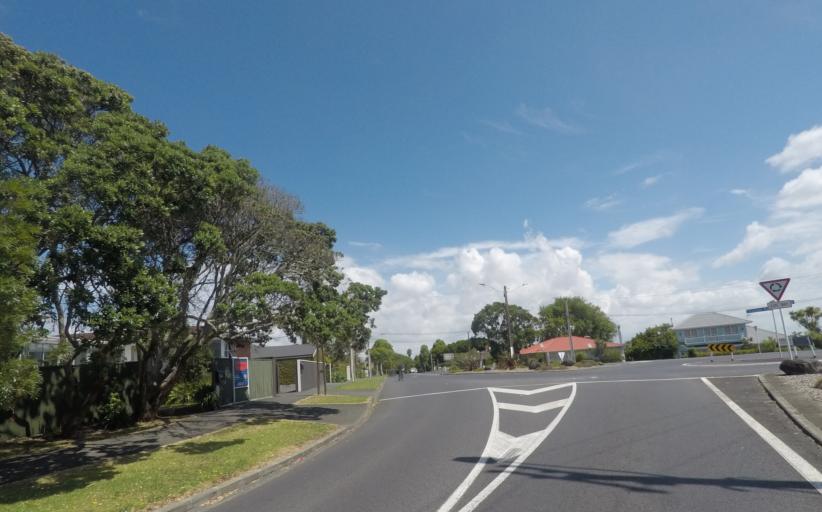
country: NZ
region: Auckland
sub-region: Auckland
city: Tamaki
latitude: -36.8744
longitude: 174.8426
